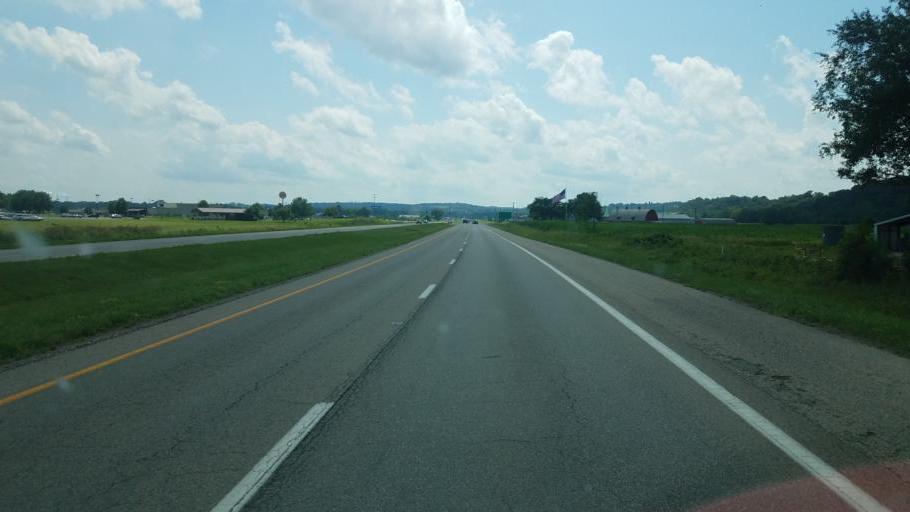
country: US
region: Ohio
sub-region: Coshocton County
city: Coshocton
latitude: 40.3011
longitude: -81.8476
